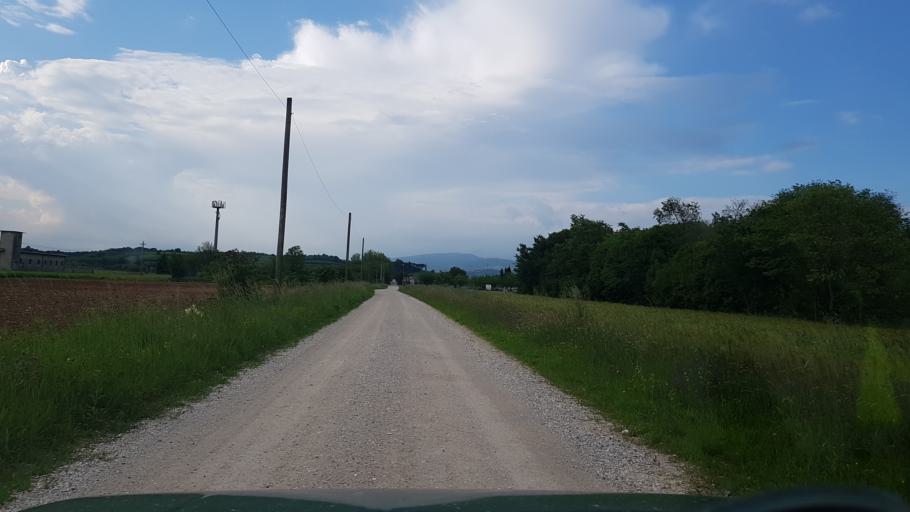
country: IT
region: Friuli Venezia Giulia
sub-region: Provincia di Gorizia
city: Mossa
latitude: 45.9273
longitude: 13.5426
